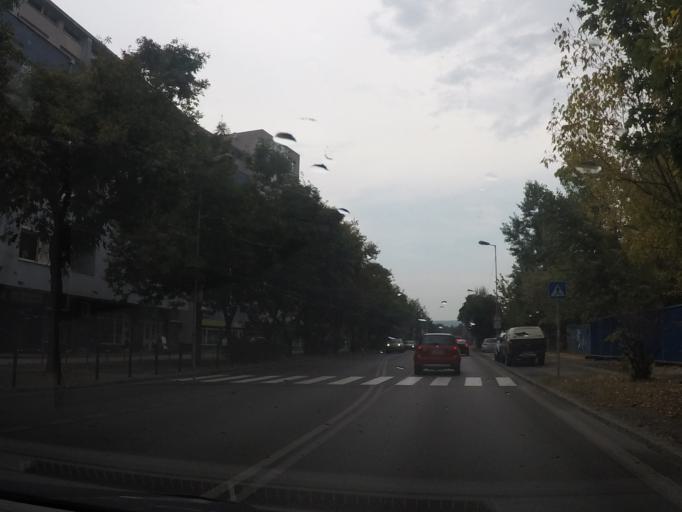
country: SK
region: Bratislavsky
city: Bratislava
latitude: 48.1554
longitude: 17.1633
